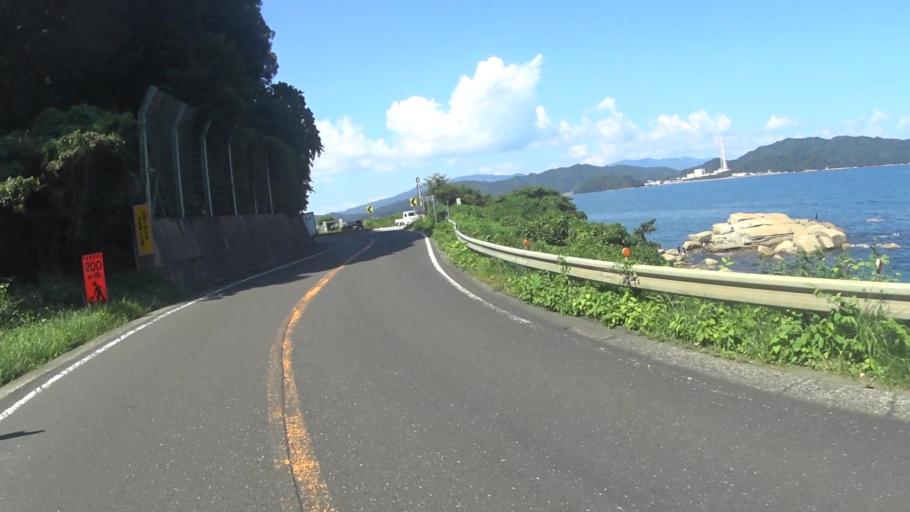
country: JP
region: Kyoto
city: Miyazu
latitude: 35.5332
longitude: 135.2642
